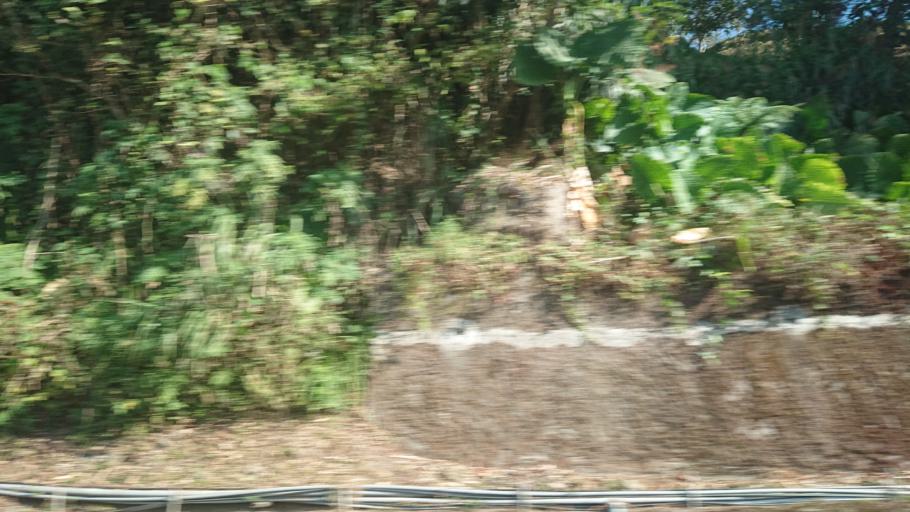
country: TW
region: Taiwan
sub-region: Chiayi
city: Jiayi Shi
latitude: 23.4719
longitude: 120.7041
